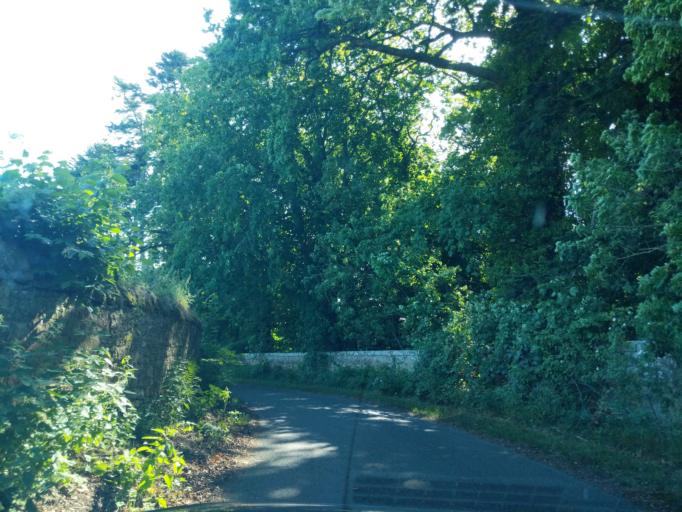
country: GB
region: Scotland
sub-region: Fife
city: Pathhead
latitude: 55.8767
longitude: -2.9714
